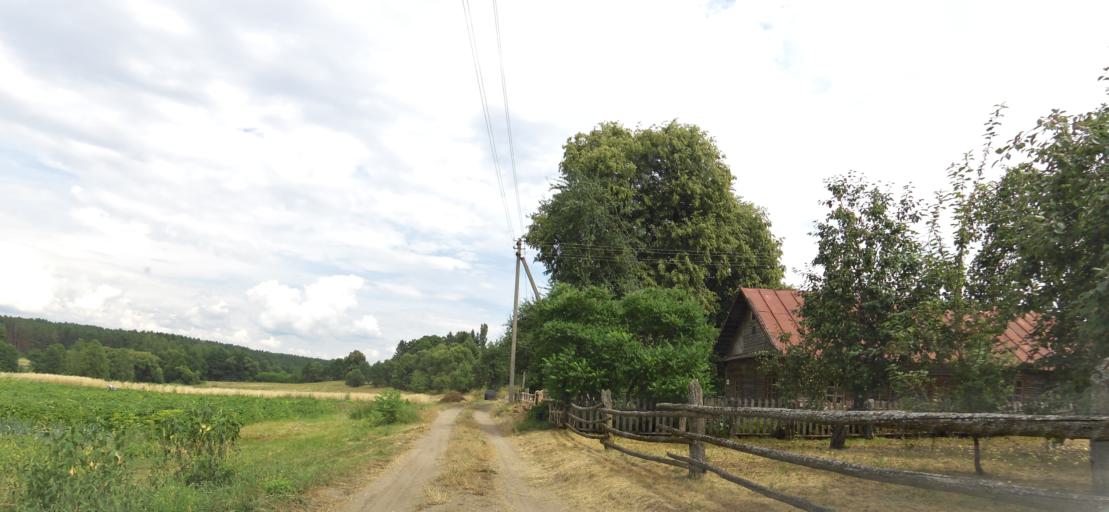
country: LT
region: Alytaus apskritis
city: Druskininkai
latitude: 53.9994
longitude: 24.2871
